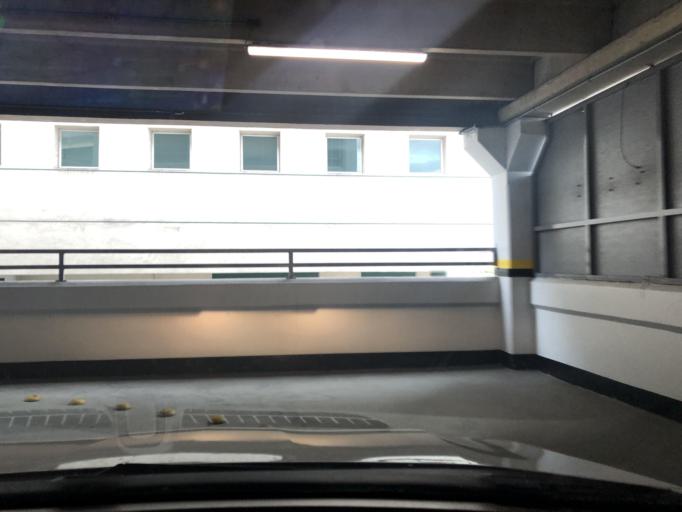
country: BR
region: Santa Catarina
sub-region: Joinville
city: Joinville
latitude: -26.3032
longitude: -48.8496
